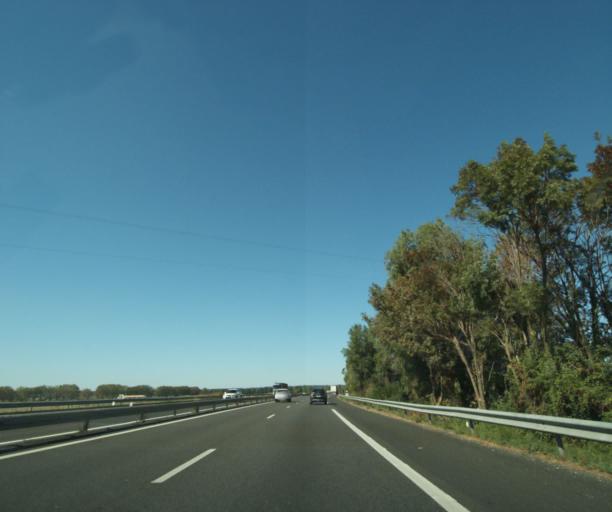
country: FR
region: Languedoc-Roussillon
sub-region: Departement du Gard
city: Bellegarde
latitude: 43.7141
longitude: 4.5132
